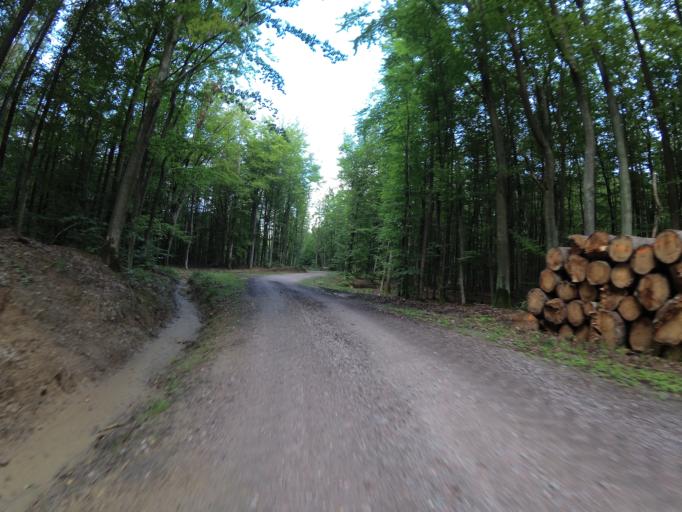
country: PL
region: Pomeranian Voivodeship
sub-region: Powiat wejherowski
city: Bojano
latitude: 54.5098
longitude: 18.4214
